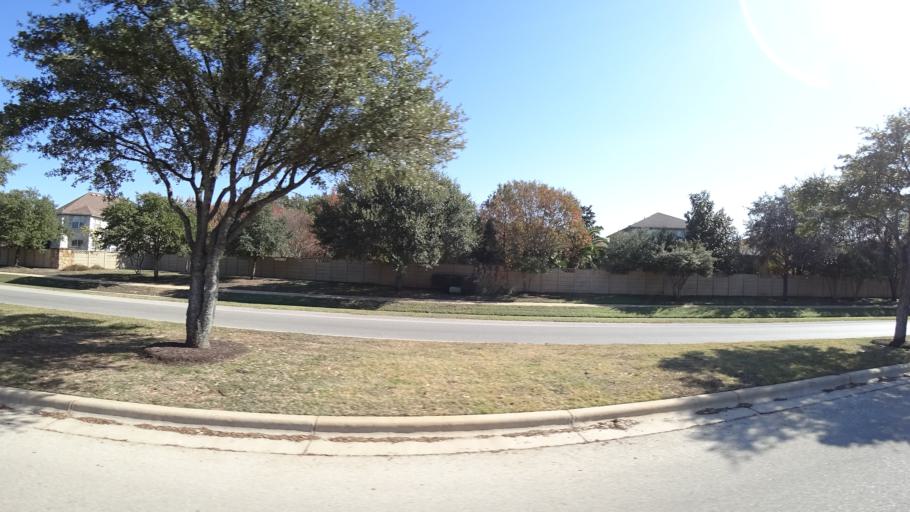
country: US
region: Texas
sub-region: Williamson County
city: Cedar Park
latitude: 30.4795
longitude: -97.8521
